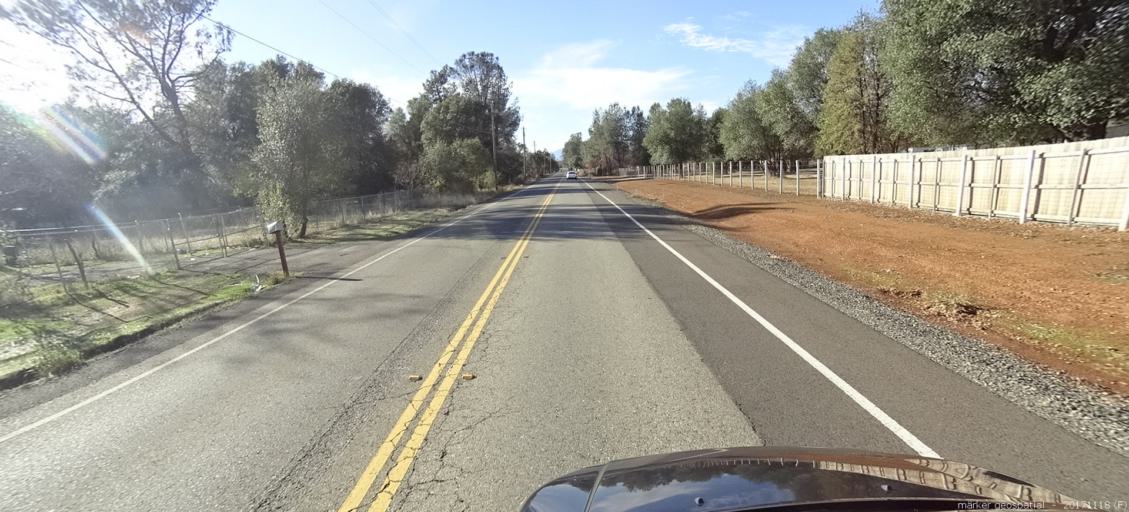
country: US
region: California
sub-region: Shasta County
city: Redding
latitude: 40.4781
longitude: -122.4344
